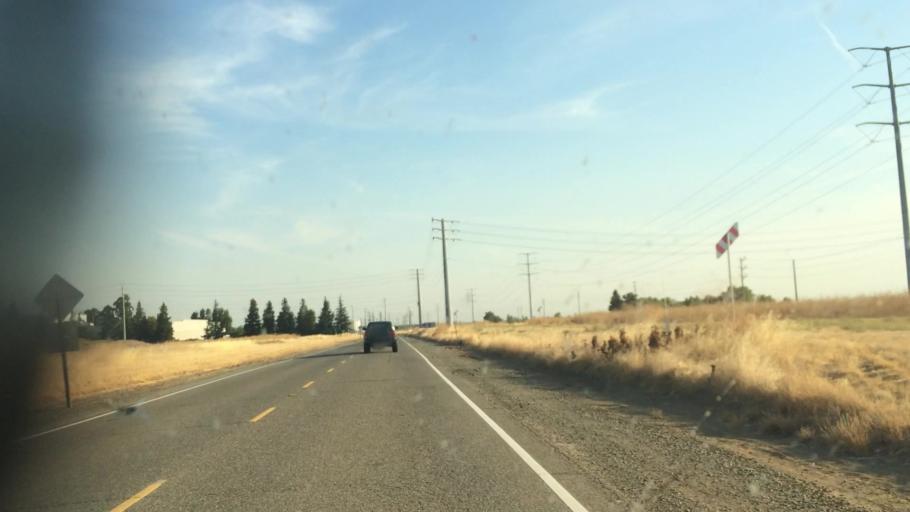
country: US
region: California
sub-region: Sacramento County
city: Laguna
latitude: 38.4423
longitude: -121.4591
